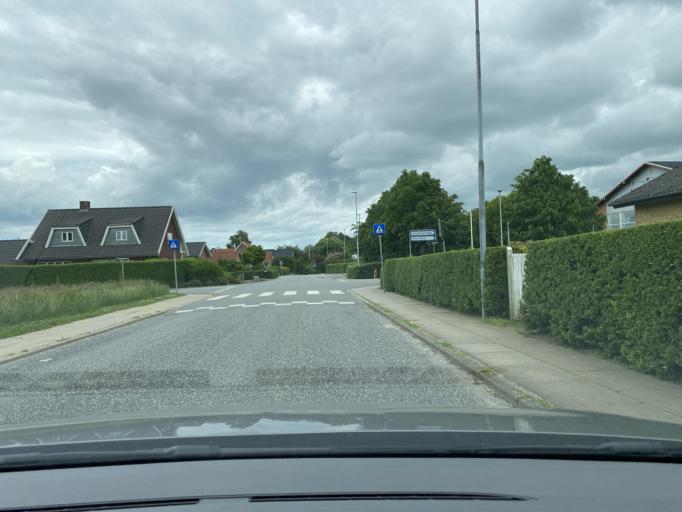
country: DK
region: South Denmark
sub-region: Vejle Kommune
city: Vejle
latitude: 55.6572
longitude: 9.5010
